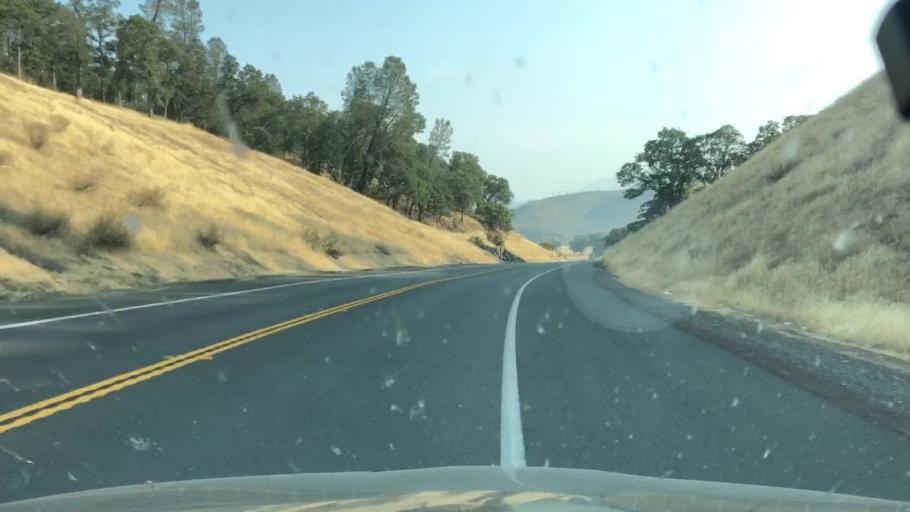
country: US
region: California
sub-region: Lake County
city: Hidden Valley Lake
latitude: 38.8135
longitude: -122.5723
